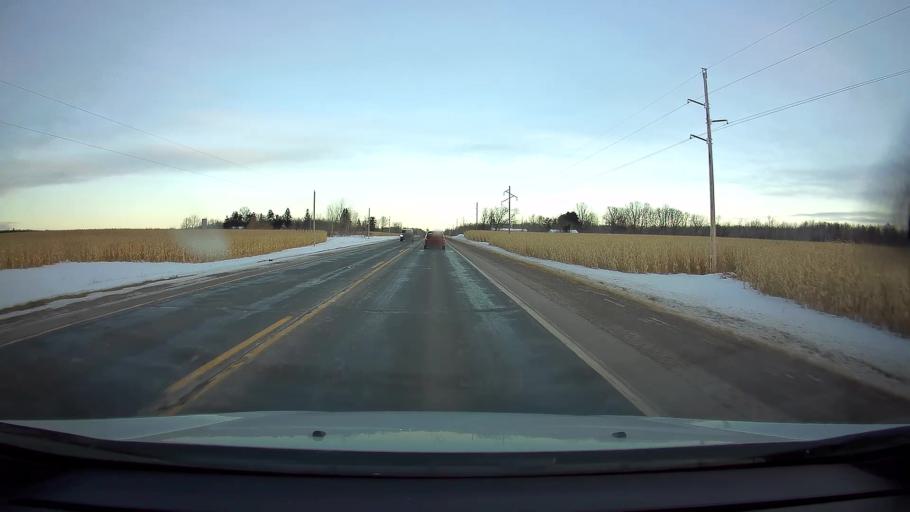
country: US
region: Wisconsin
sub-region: Barron County
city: Turtle Lake
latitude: 45.3501
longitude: -92.1669
